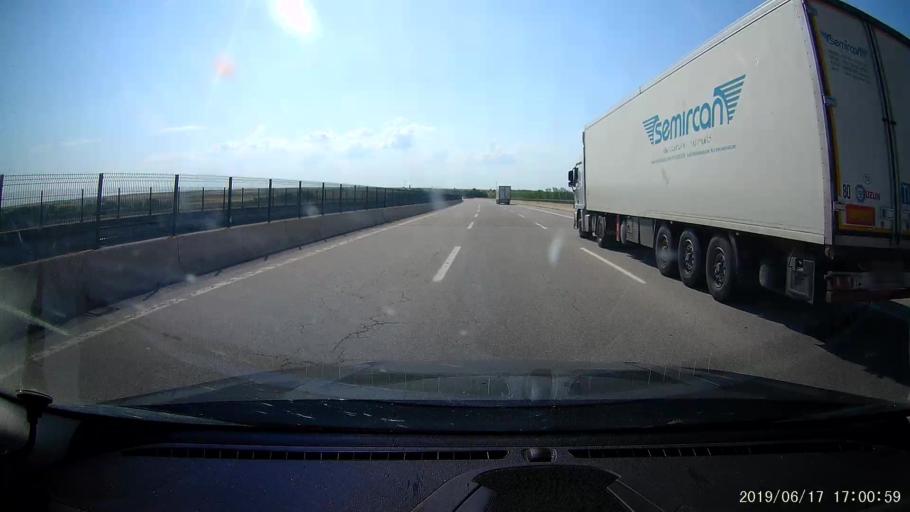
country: TR
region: Edirne
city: Haskoy
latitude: 41.6260
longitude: 26.8160
